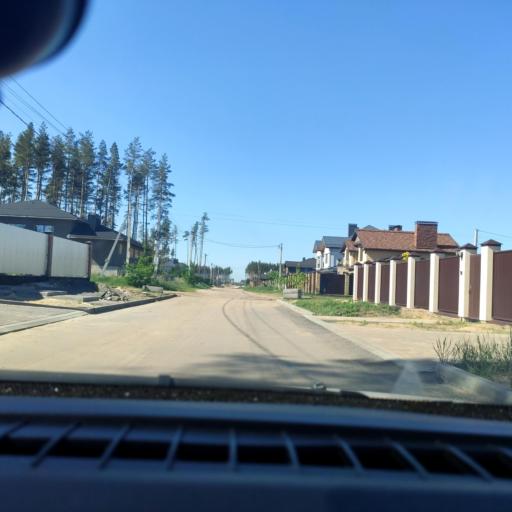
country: RU
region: Voronezj
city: Podgornoye
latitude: 51.7813
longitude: 39.1472
